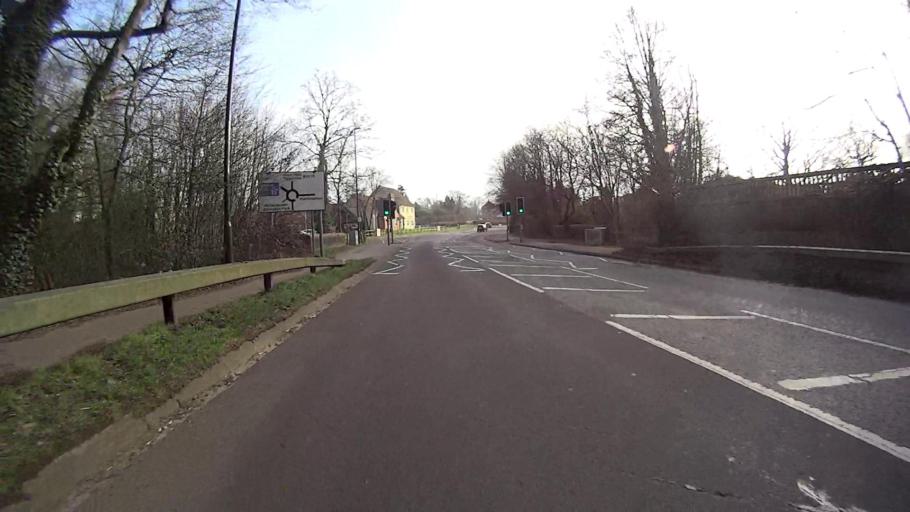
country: GB
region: England
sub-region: West Sussex
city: Maidenbower
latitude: 51.1084
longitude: -0.1446
